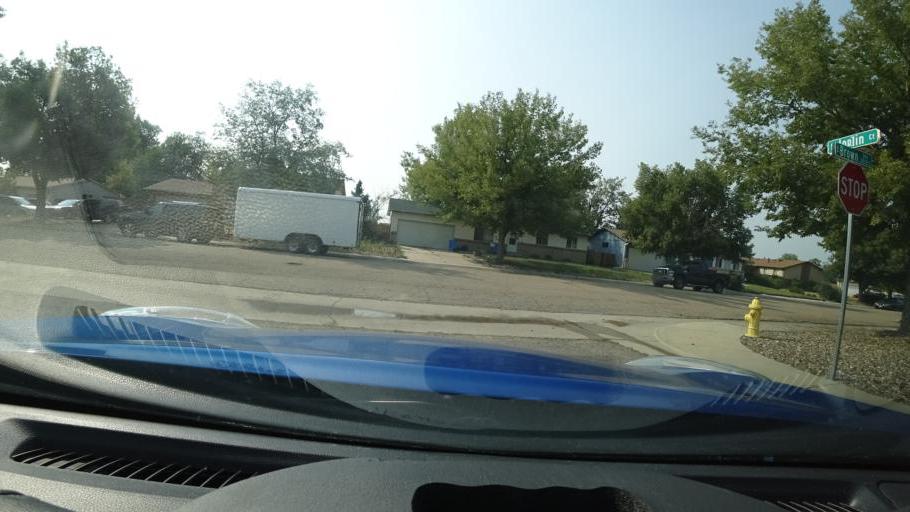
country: US
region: Colorado
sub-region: Adams County
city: Aurora
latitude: 39.6647
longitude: -104.8044
